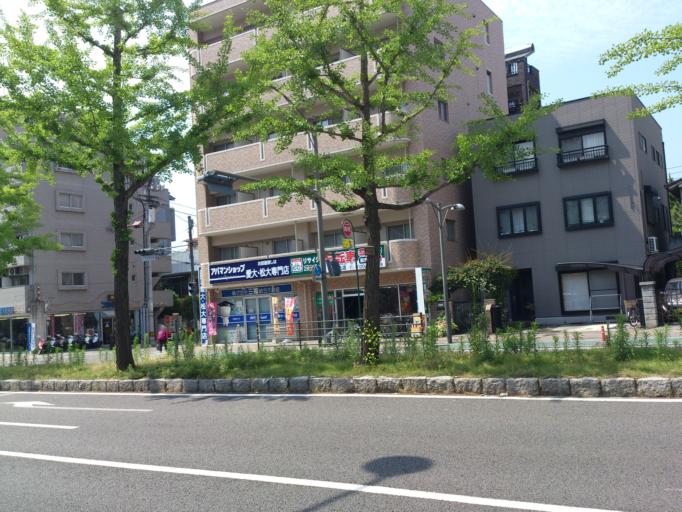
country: JP
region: Ehime
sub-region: Shikoku-chuo Shi
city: Matsuyama
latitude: 33.8474
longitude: 132.7699
